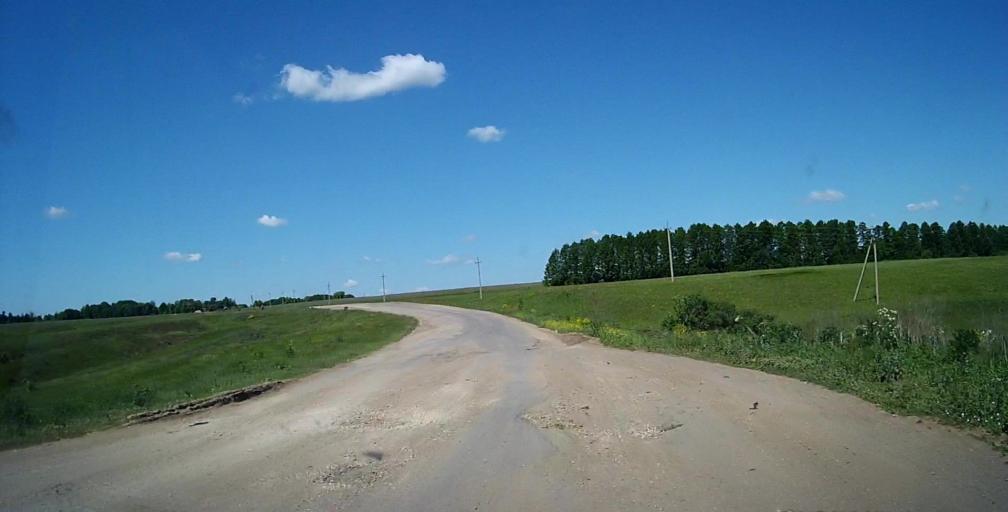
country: RU
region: Tula
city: Kurkino
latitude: 53.2064
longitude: 38.6069
